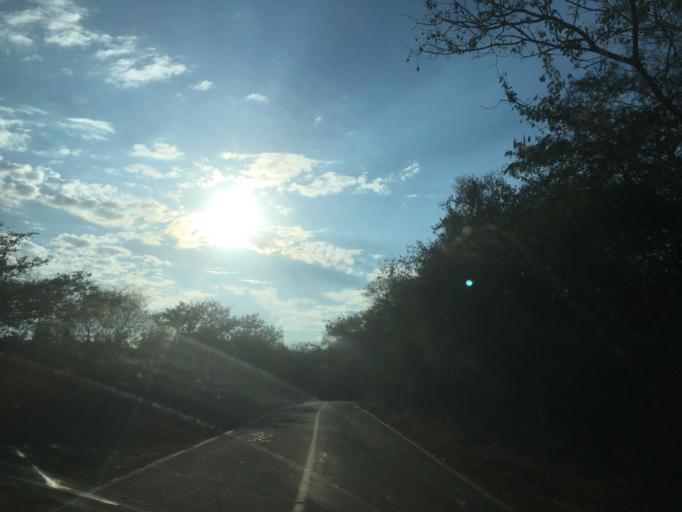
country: CO
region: Santander
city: Barichara
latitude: 6.6379
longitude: -73.2067
